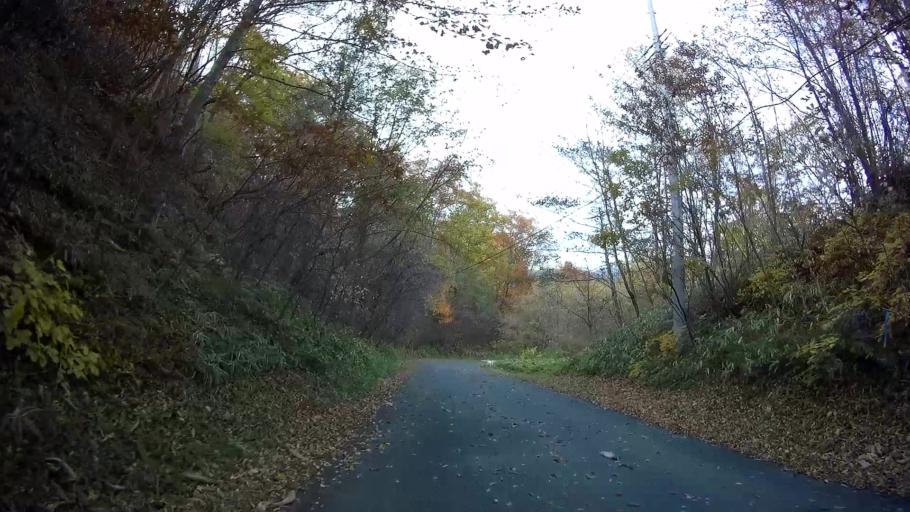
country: JP
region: Gunma
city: Nakanojomachi
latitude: 36.6372
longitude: 138.6422
